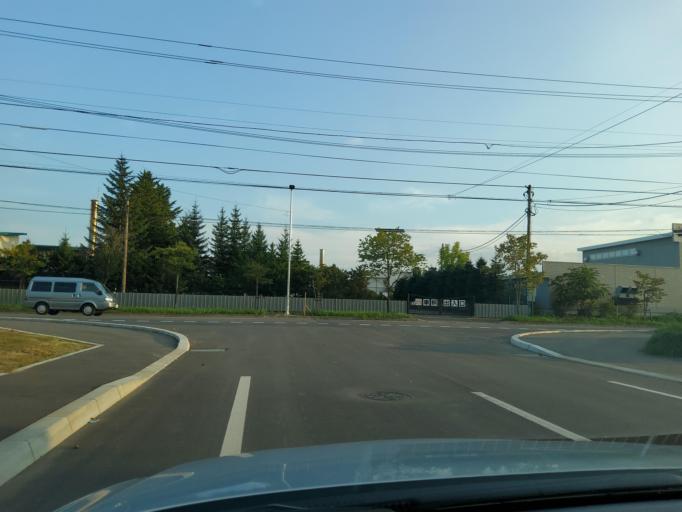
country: JP
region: Hokkaido
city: Obihiro
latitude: 42.9337
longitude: 143.1536
